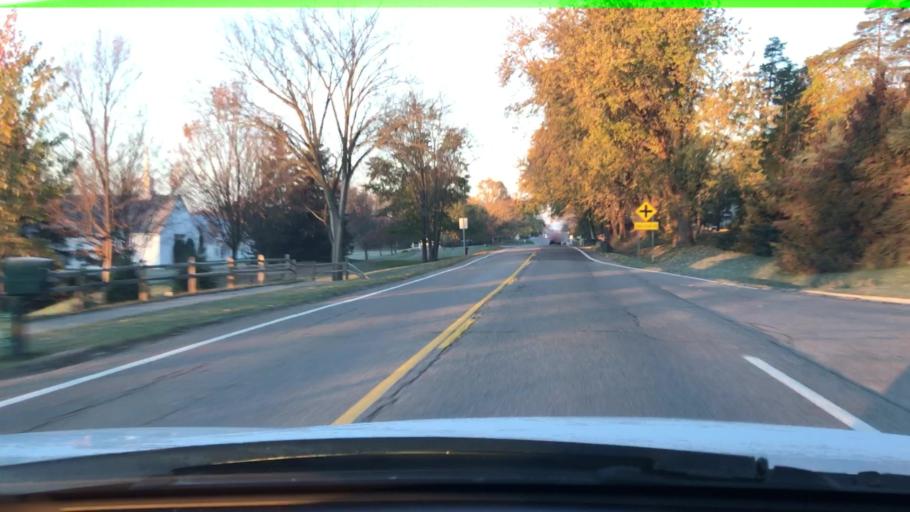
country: US
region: Michigan
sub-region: Oakland County
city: Clarkston
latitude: 42.7523
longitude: -83.3663
